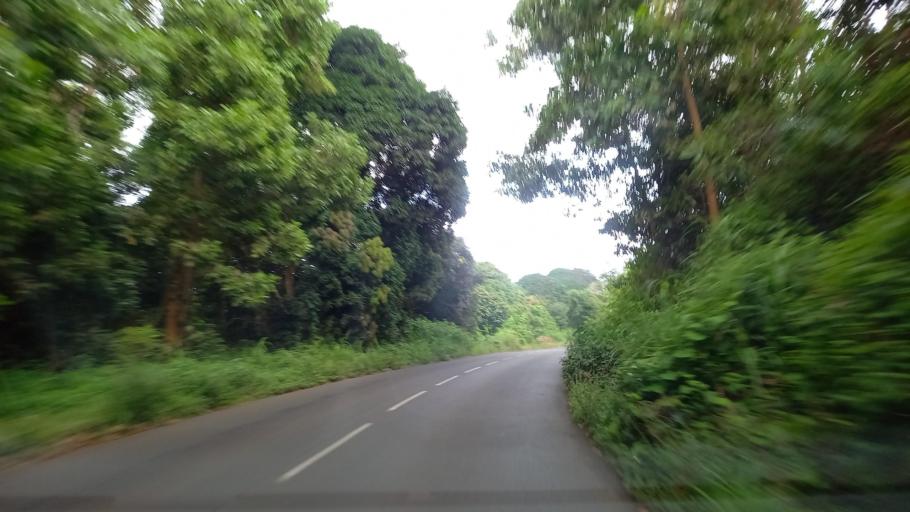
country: YT
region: Tsingoni
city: Tsingoni
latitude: -12.7865
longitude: 45.1518
